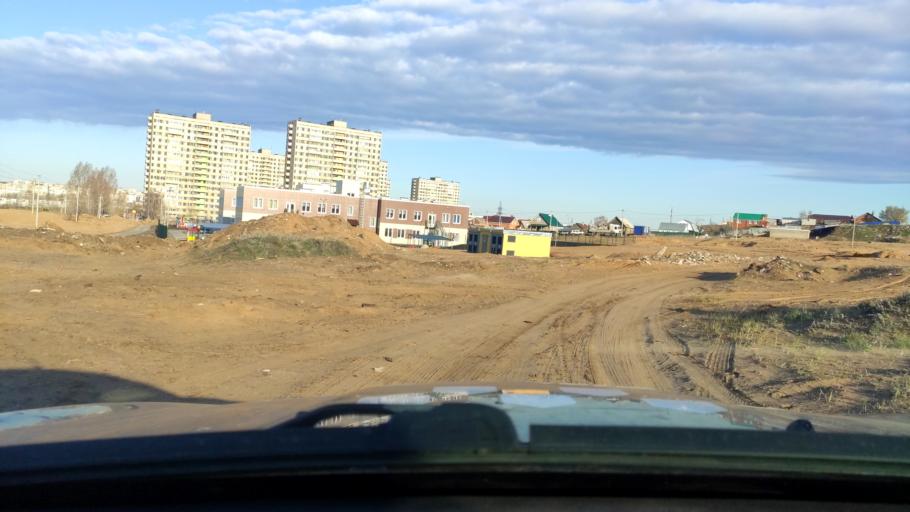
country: RU
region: Samara
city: Zhigulevsk
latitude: 53.4794
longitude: 49.5318
